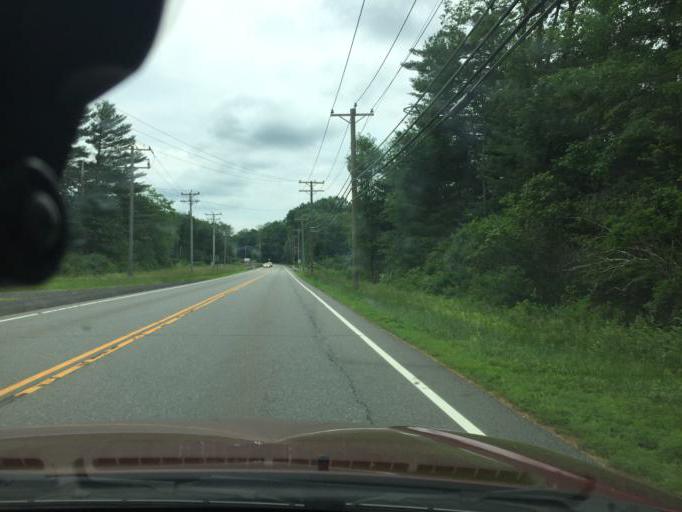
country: US
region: Connecticut
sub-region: Litchfield County
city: Litchfield
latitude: 41.7301
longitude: -73.2181
